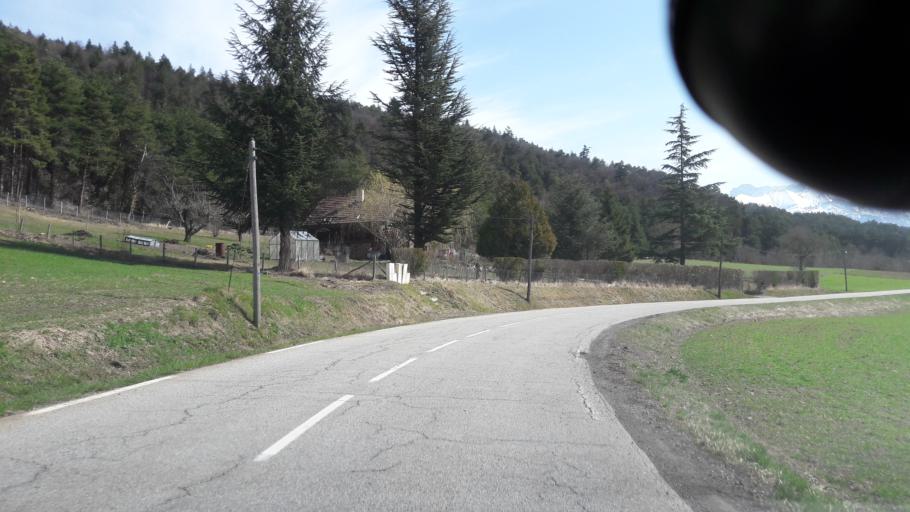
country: FR
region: Rhone-Alpes
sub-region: Departement de l'Isere
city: La Motte-Saint-Martin
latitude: 44.8847
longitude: 5.6448
